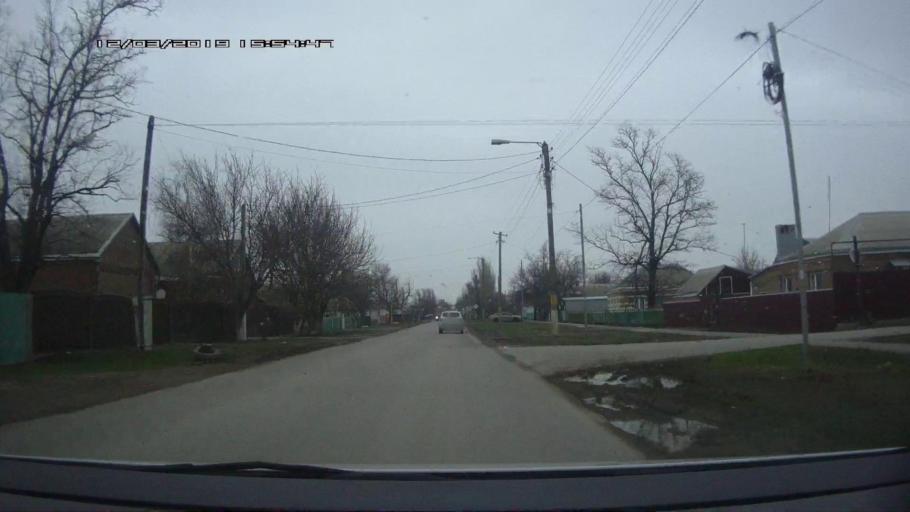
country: RU
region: Rostov
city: Novobataysk
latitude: 46.8927
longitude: 39.7784
